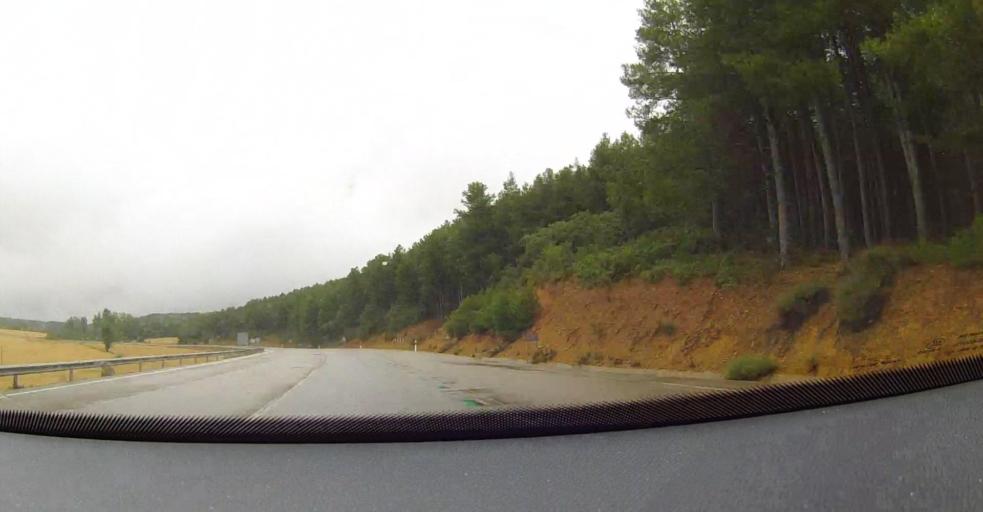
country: ES
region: Castille and Leon
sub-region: Provincia de Palencia
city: Saldana
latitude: 42.5508
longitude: -4.7326
